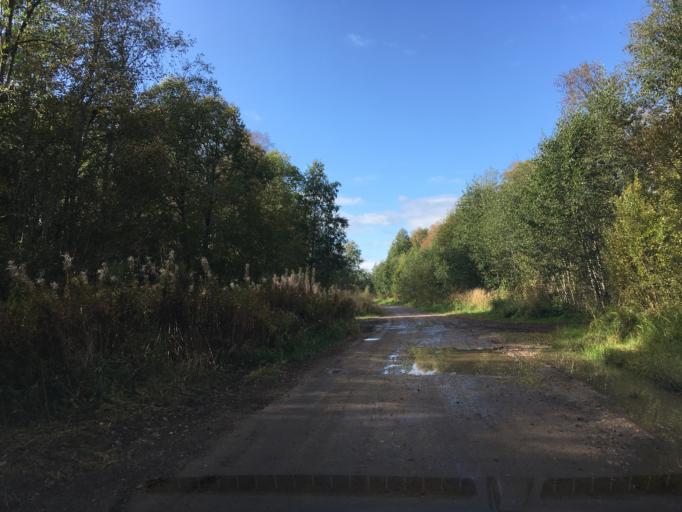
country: EE
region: Harju
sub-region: Saku vald
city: Saku
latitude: 59.3358
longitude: 24.6671
